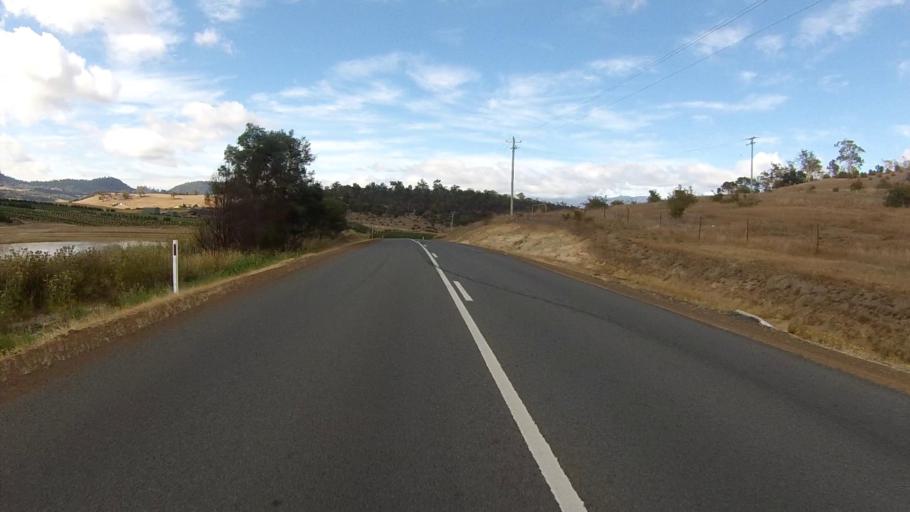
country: AU
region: Tasmania
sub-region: Brighton
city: Old Beach
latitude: -42.7389
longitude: 147.2882
